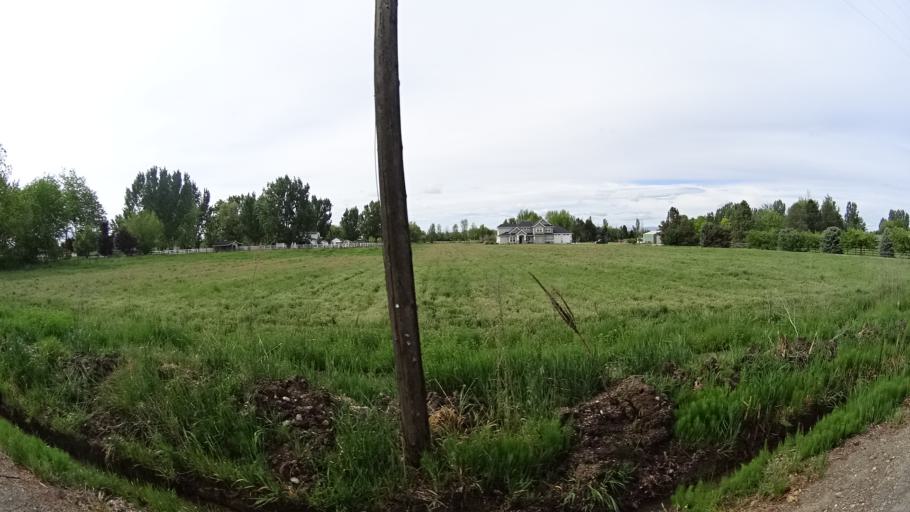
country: US
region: Idaho
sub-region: Ada County
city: Eagle
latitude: 43.7209
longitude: -116.3952
